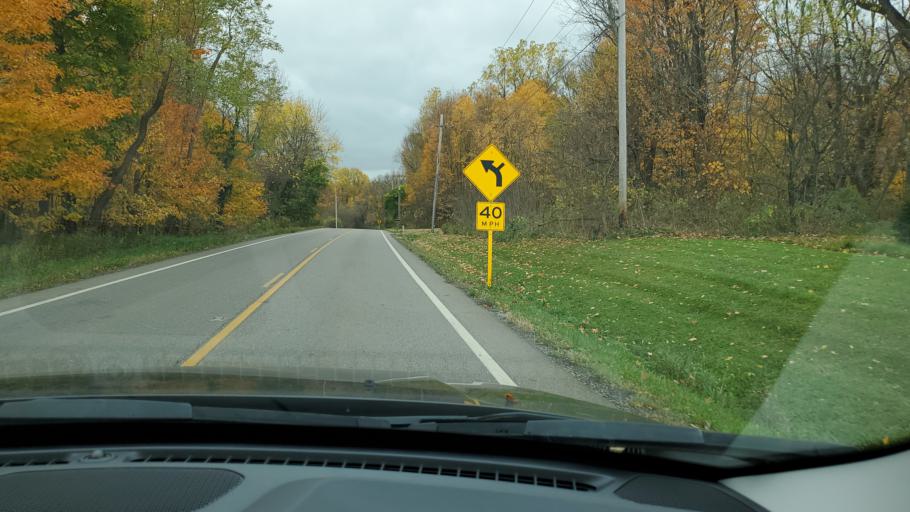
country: US
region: Ohio
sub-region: Mahoning County
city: Boardman
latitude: 40.9523
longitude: -80.6415
